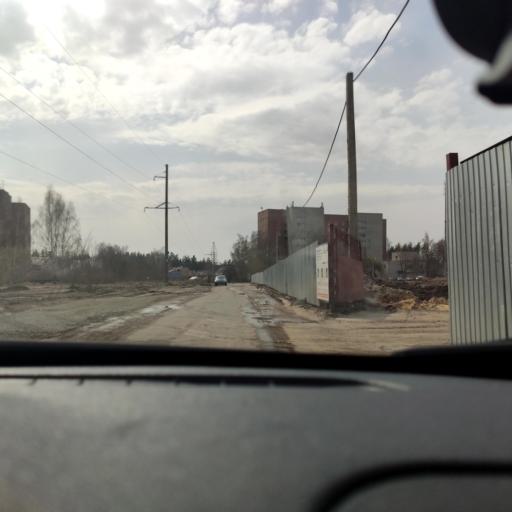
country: RU
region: Voronezj
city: Podgornoye
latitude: 51.7587
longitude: 39.1749
